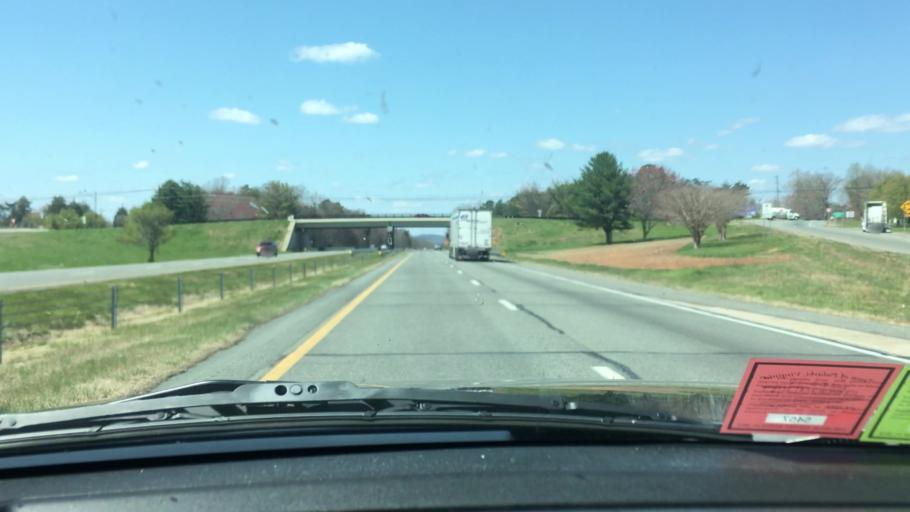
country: US
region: North Carolina
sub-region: Surry County
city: Pilot Mountain
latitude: 36.3746
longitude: -80.4859
